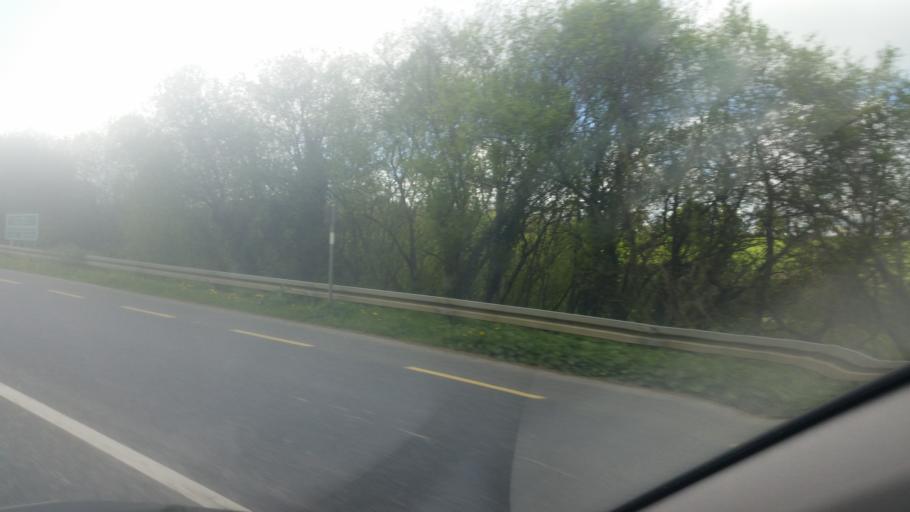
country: IE
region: Leinster
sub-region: Loch Garman
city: Enniscorthy
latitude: 52.4661
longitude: -6.5607
